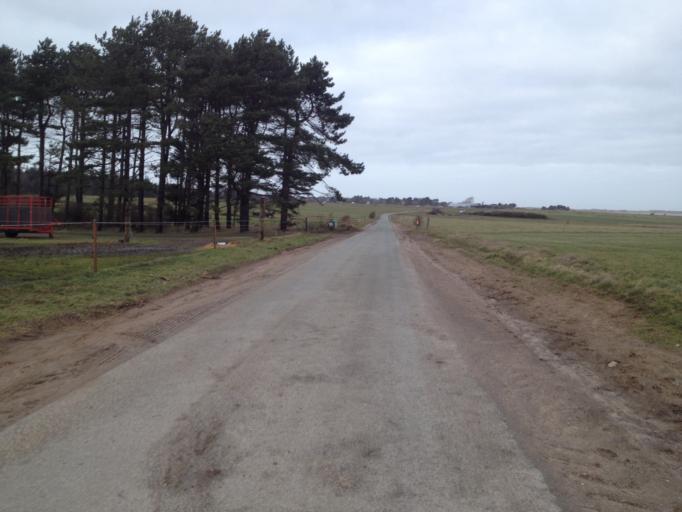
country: DE
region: Schleswig-Holstein
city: Norddorf
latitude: 54.6687
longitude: 8.3432
